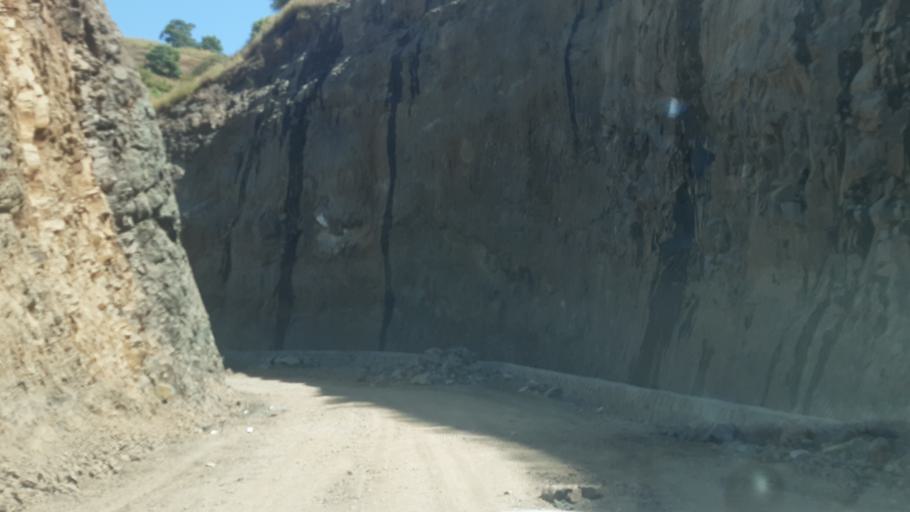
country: ET
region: Amhara
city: Dabat
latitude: 13.1687
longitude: 37.6059
